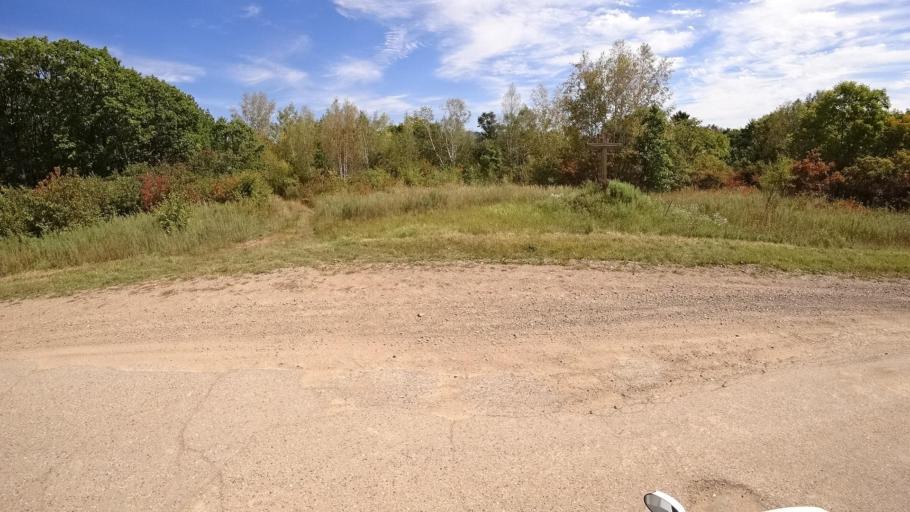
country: RU
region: Primorskiy
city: Yakovlevka
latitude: 44.7055
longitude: 133.6422
